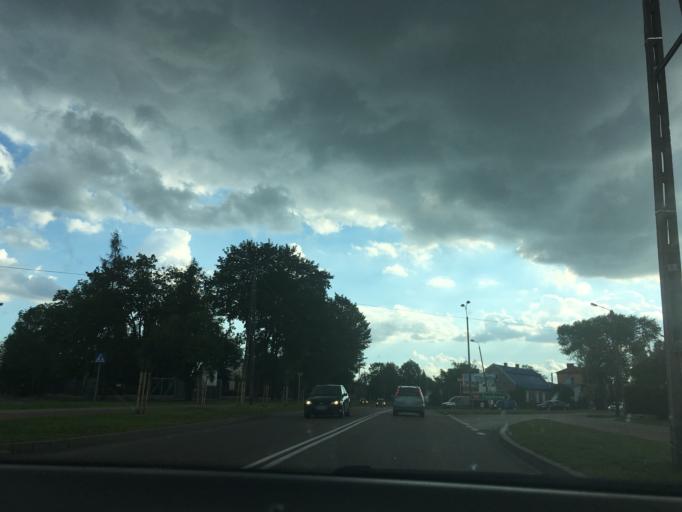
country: PL
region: Podlasie
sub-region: Powiat bielski
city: Bielsk Podlaski
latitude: 52.7621
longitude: 23.1831
